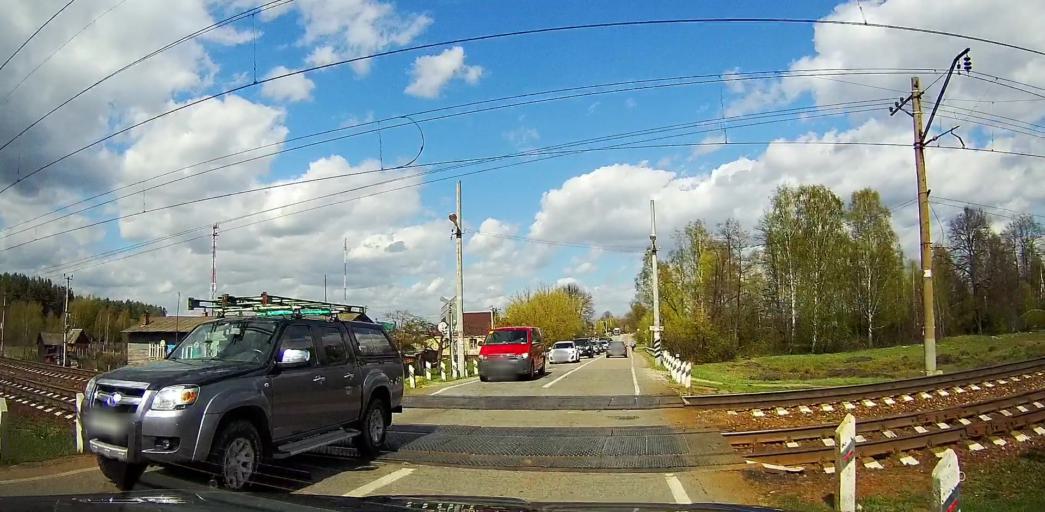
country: RU
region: Moskovskaya
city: Davydovo
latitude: 55.5730
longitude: 38.8192
